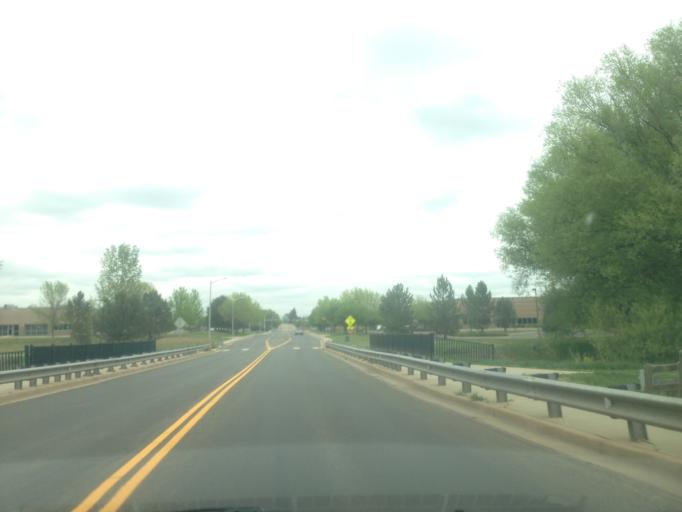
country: US
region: Colorado
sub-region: Boulder County
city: Longmont
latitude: 40.1344
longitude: -105.1215
